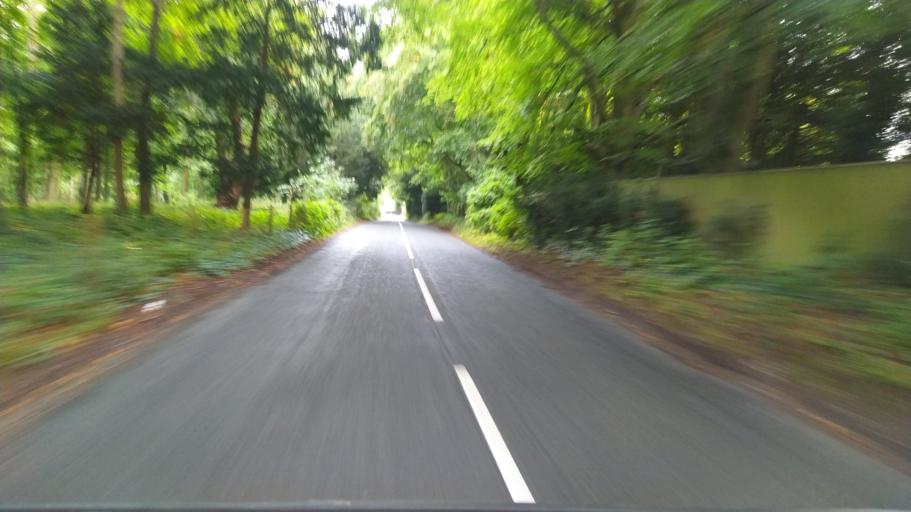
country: GB
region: England
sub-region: Hampshire
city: East Dean
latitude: 51.0756
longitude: -1.5565
